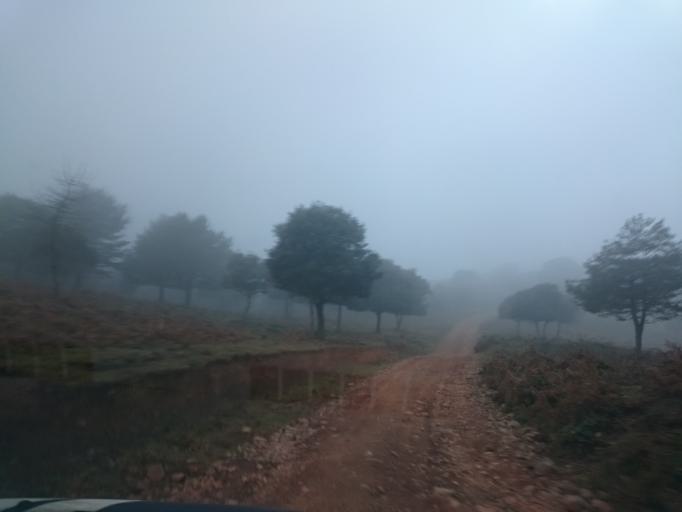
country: ES
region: Catalonia
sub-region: Provincia de Barcelona
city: Tagamanent
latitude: 41.7503
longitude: 2.3130
